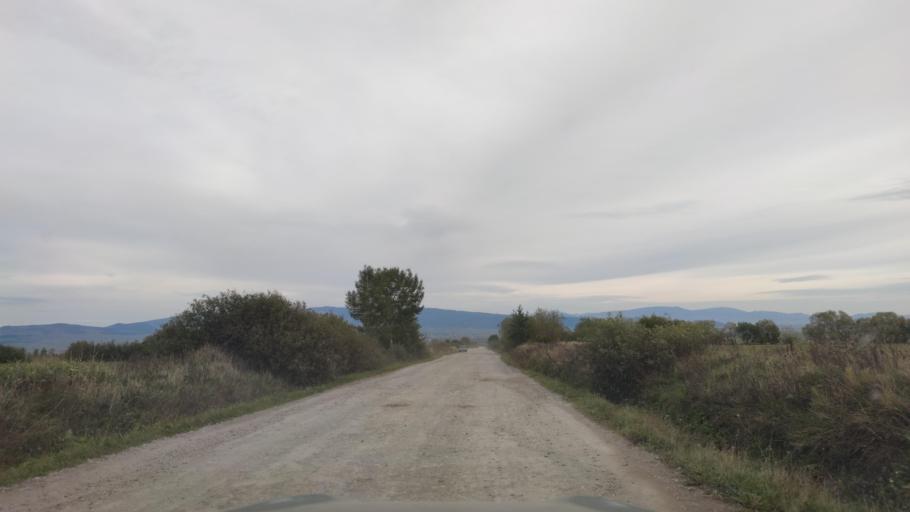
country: RO
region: Harghita
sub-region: Comuna Remetea
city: Remetea
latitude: 46.8103
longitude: 25.3943
